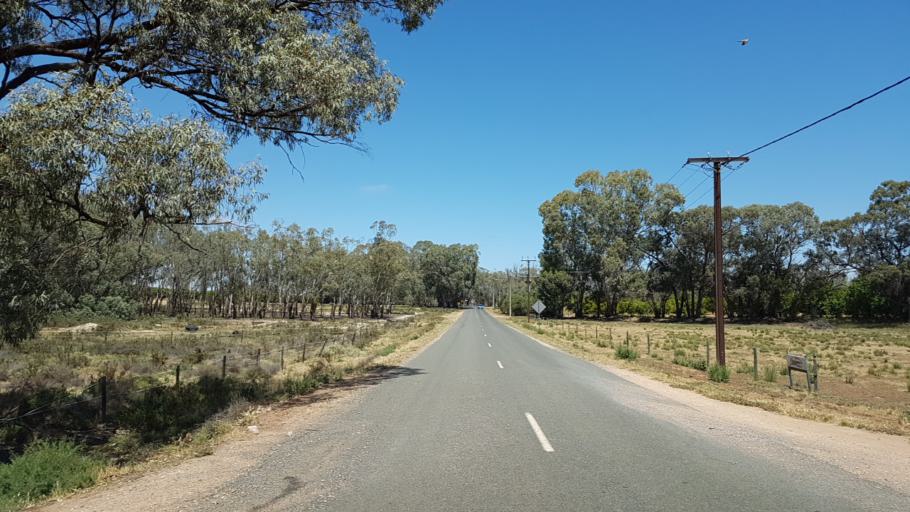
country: AU
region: South Australia
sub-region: Loxton Waikerie
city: Waikerie
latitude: -34.1657
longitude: 140.0287
